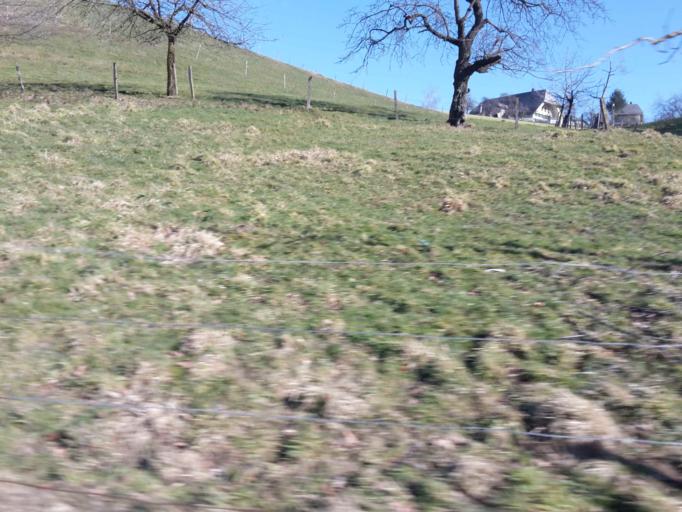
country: CH
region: Bern
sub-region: Emmental District
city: Durrenroth
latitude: 47.1102
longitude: 7.7767
